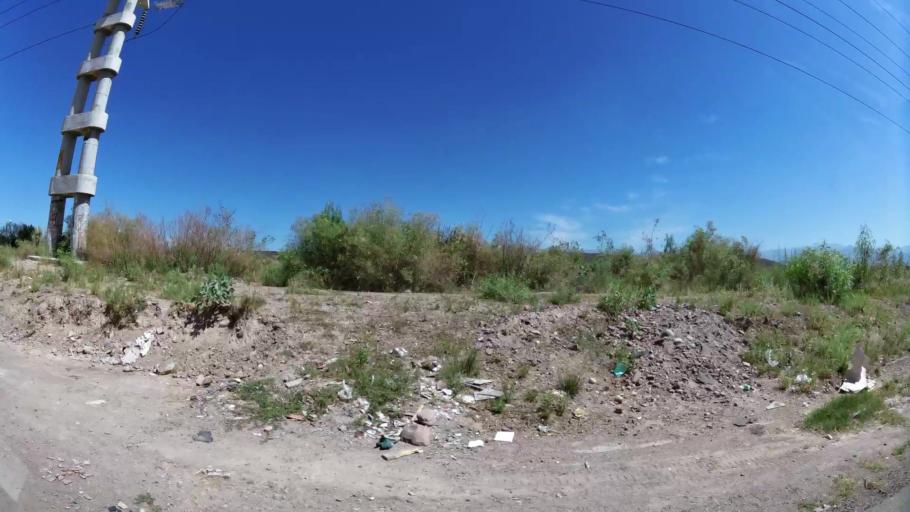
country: AR
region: Mendoza
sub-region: Departamento de Godoy Cruz
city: Godoy Cruz
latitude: -32.9489
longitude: -68.8745
